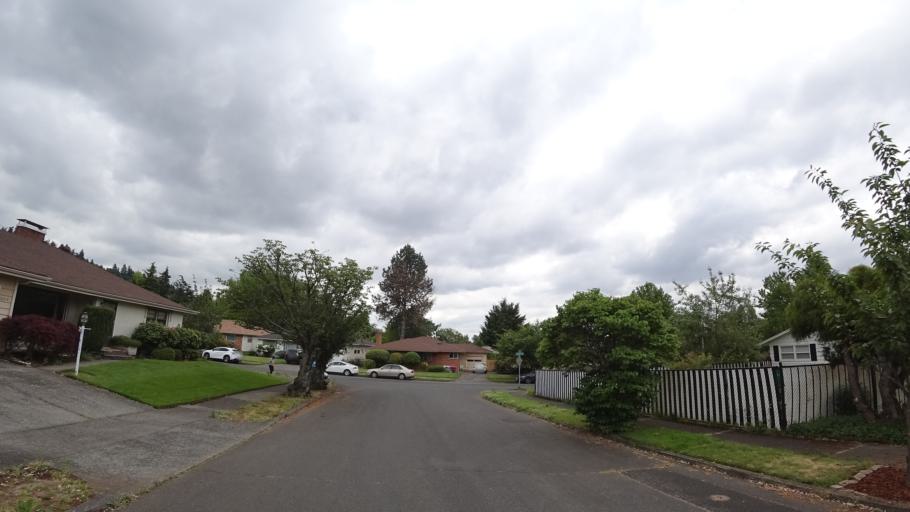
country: US
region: Oregon
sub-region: Multnomah County
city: Lents
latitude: 45.5070
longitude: -122.5559
